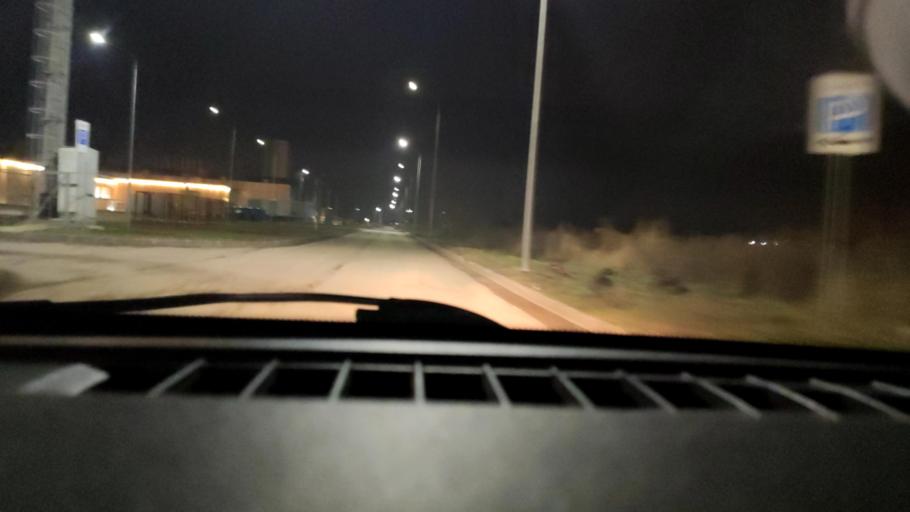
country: RU
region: Samara
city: Samara
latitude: 53.1413
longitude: 50.1715
